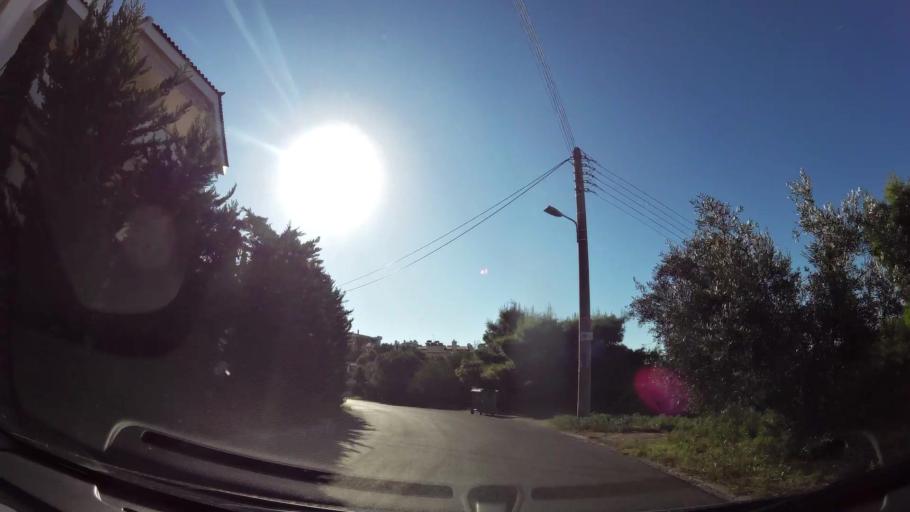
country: GR
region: Attica
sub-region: Nomarchia Athinas
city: Glyfada
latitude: 37.8585
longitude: 23.7704
